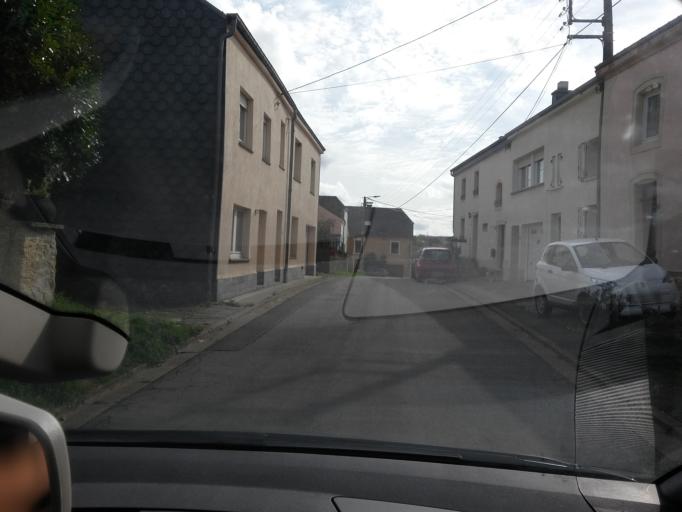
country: BE
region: Wallonia
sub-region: Province du Luxembourg
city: Arlon
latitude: 49.6972
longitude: 5.7916
